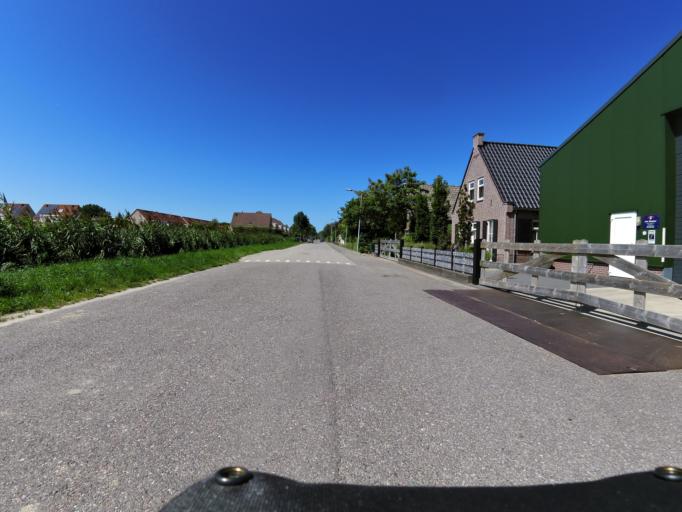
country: NL
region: South Holland
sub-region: Gemeente Goeree-Overflakkee
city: Goedereede
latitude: 51.7997
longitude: 4.0274
